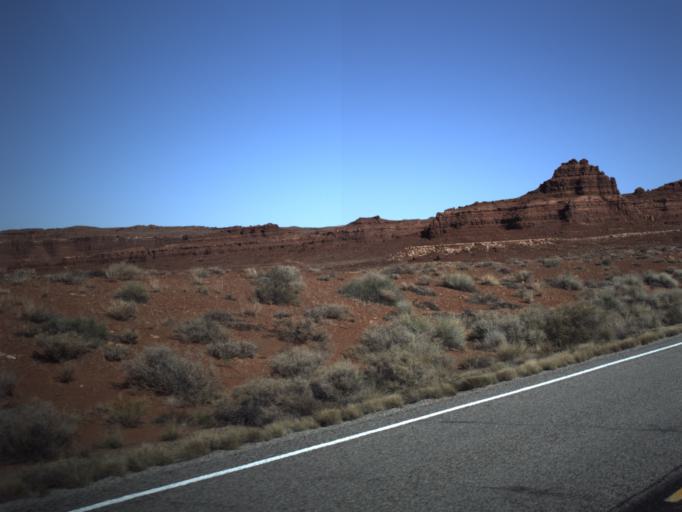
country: US
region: Utah
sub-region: San Juan County
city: Blanding
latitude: 37.8467
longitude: -110.3547
